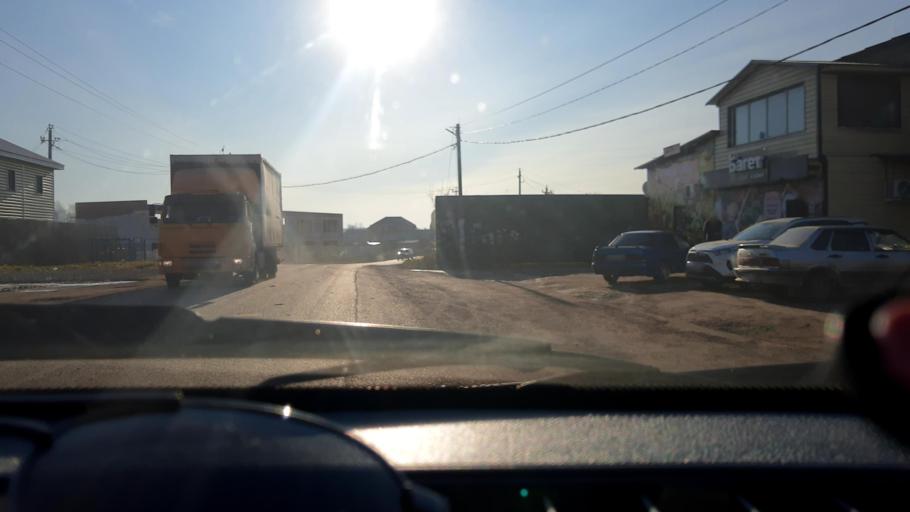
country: RU
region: Bashkortostan
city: Mikhaylovka
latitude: 54.8030
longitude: 55.8795
